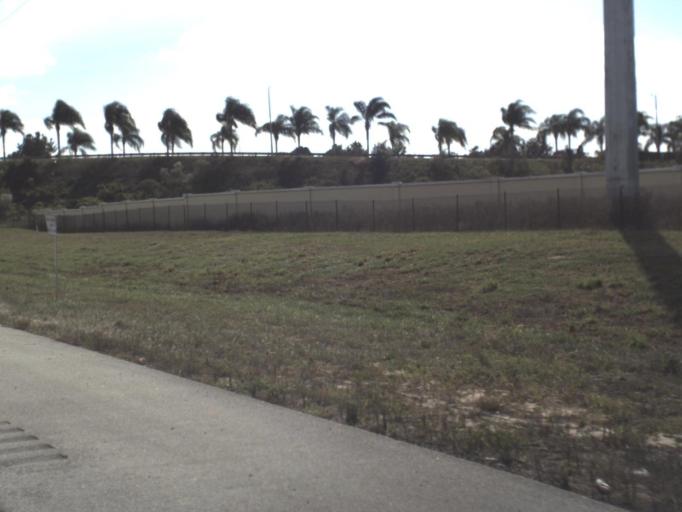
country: US
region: Florida
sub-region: Polk County
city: Citrus Ridge
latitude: 28.3198
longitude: -81.6101
